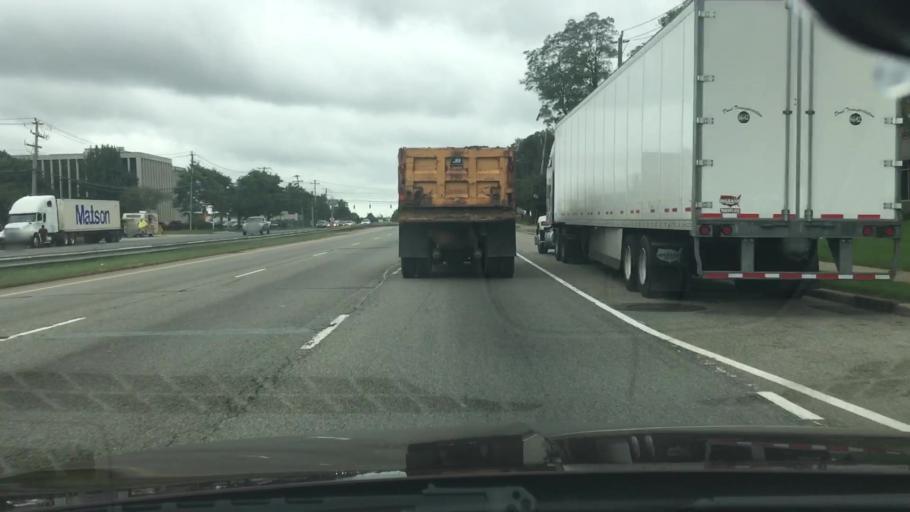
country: US
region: New York
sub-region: Suffolk County
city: Melville
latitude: 40.7652
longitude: -73.4237
